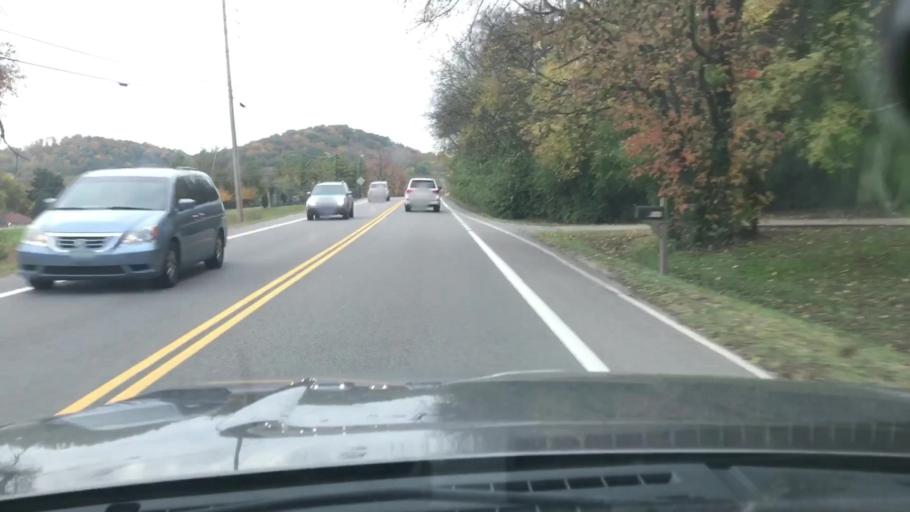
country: US
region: Tennessee
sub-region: Williamson County
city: Franklin
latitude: 36.0005
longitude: -86.8854
